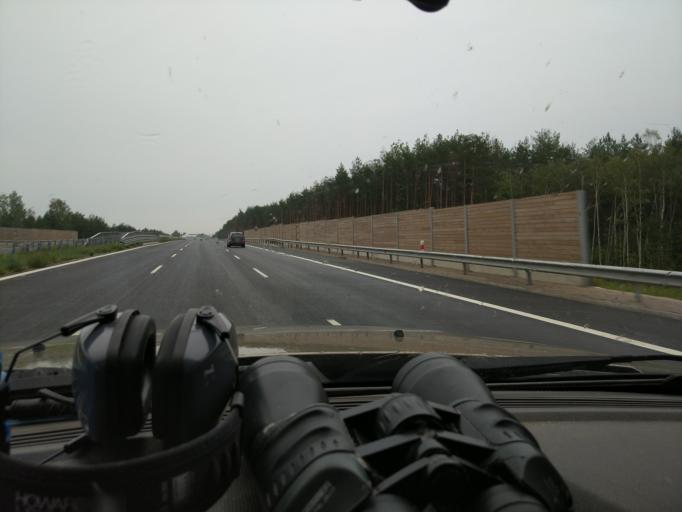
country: PL
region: Masovian Voivodeship
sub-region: Powiat wolominski
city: Radzymin
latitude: 52.3830
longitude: 21.1912
